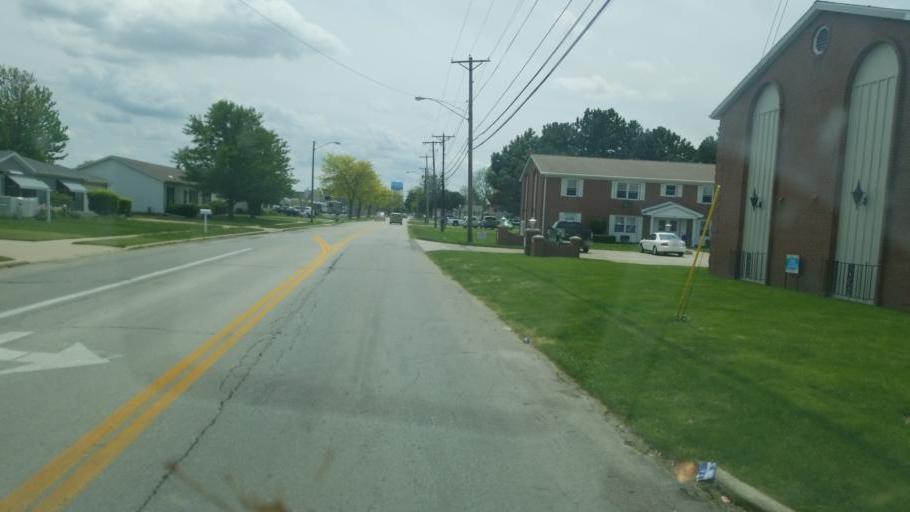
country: US
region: Ohio
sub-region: Sandusky County
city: Fremont
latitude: 41.3603
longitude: -83.1320
